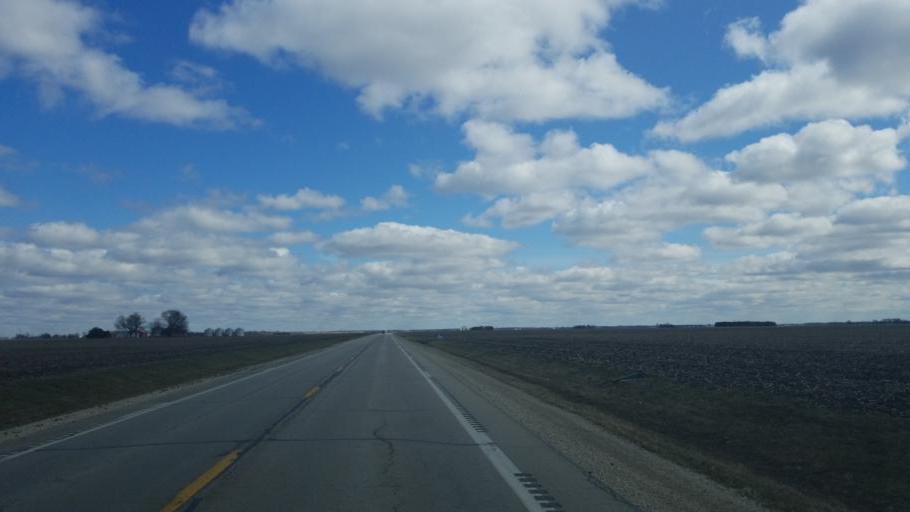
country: US
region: Illinois
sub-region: Douglas County
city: Villa Grove
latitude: 39.7919
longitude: -88.1293
